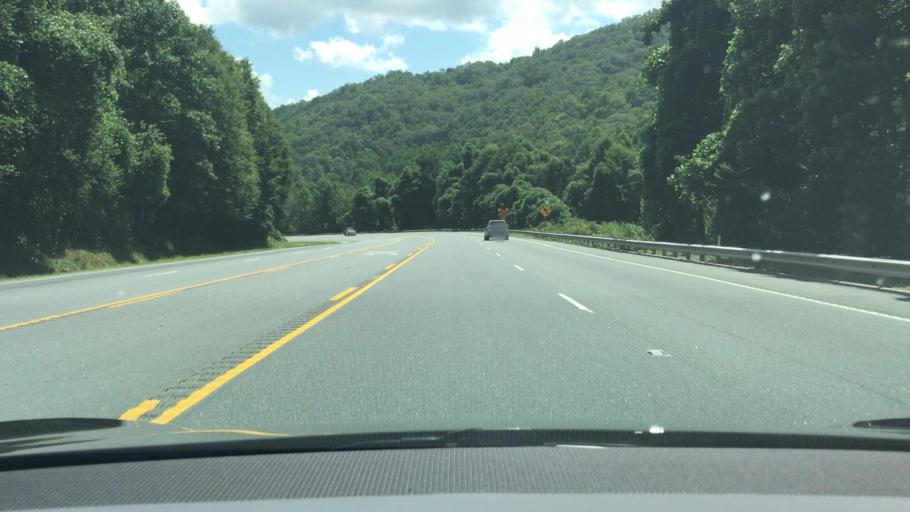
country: US
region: North Carolina
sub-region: Macon County
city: Franklin
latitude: 35.2600
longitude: -83.3032
